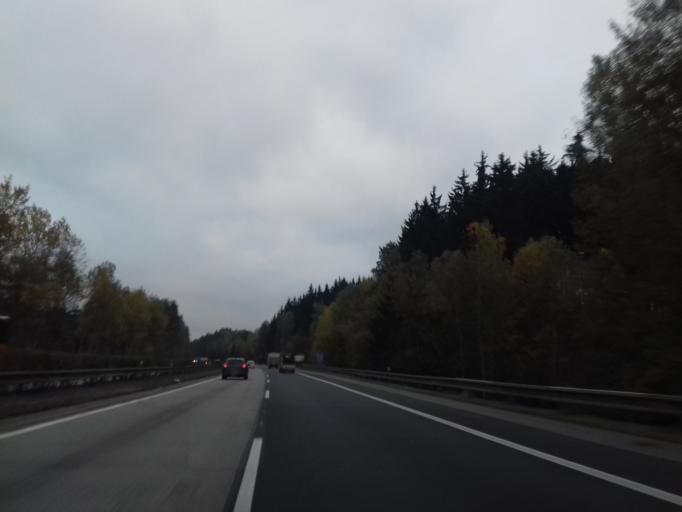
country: CZ
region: Central Bohemia
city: Divisov
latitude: 49.8124
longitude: 14.8819
